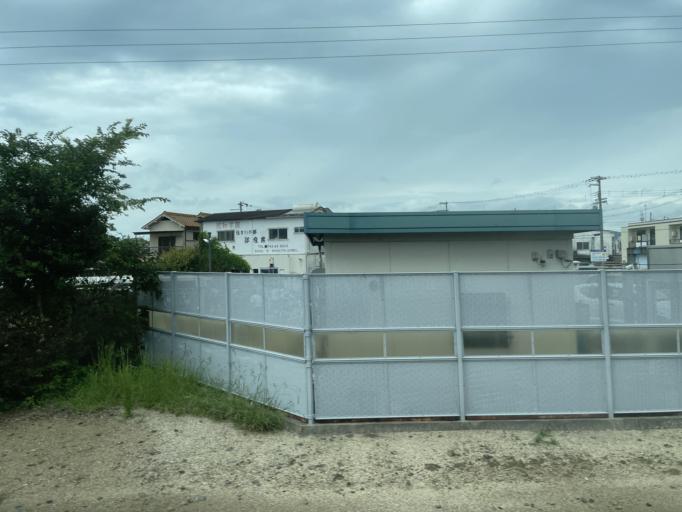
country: JP
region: Osaka
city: Izumi
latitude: 34.4666
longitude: 135.4063
